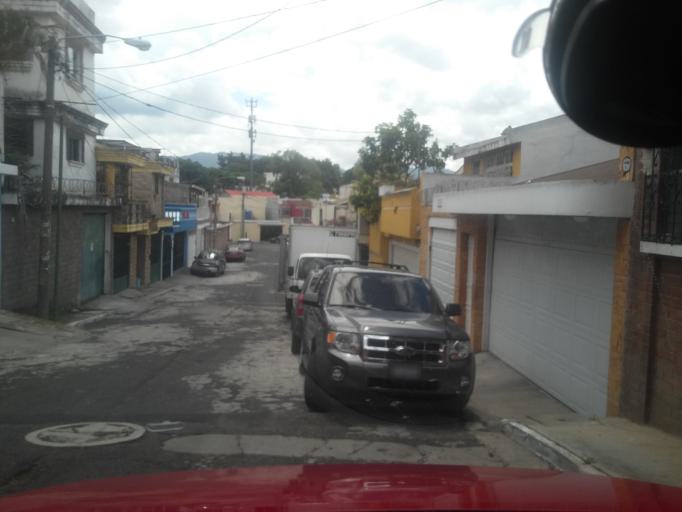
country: GT
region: Guatemala
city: Mixco
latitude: 14.6434
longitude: -90.5660
